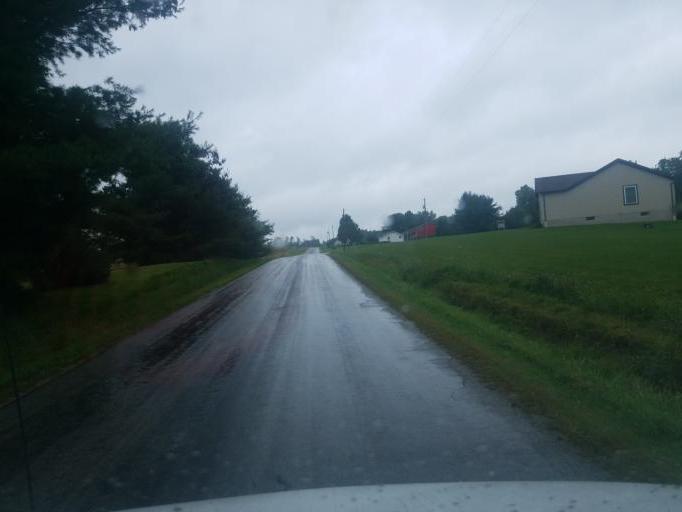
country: US
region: Ohio
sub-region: Wayne County
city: West Salem
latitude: 40.9385
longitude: -82.0351
